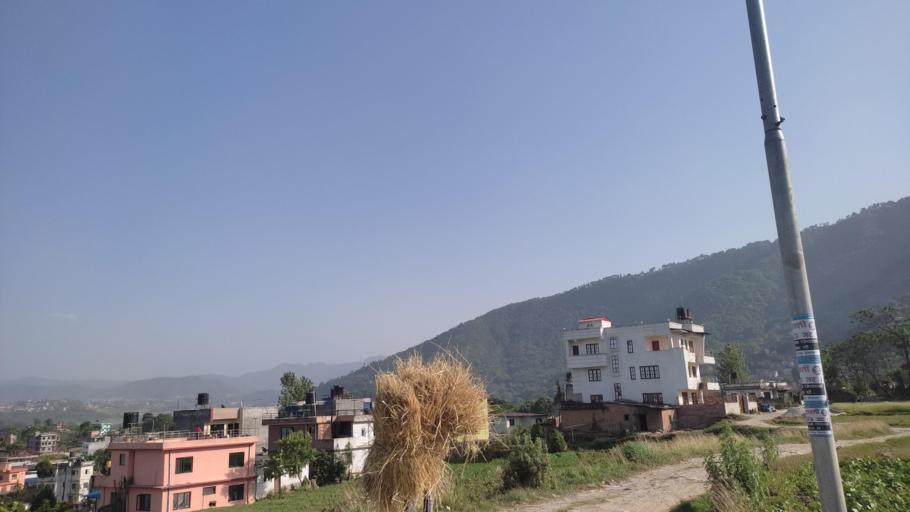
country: NP
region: Central Region
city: Kirtipur
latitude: 27.6519
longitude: 85.2815
